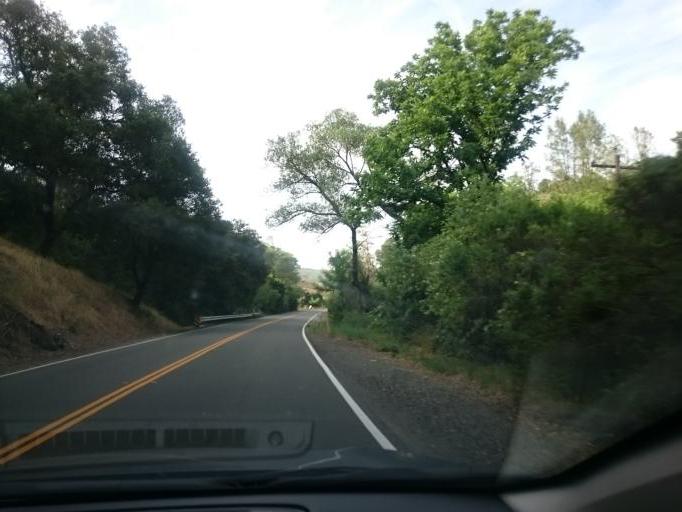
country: US
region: California
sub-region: Napa County
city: Yountville
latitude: 38.5063
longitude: -122.2772
